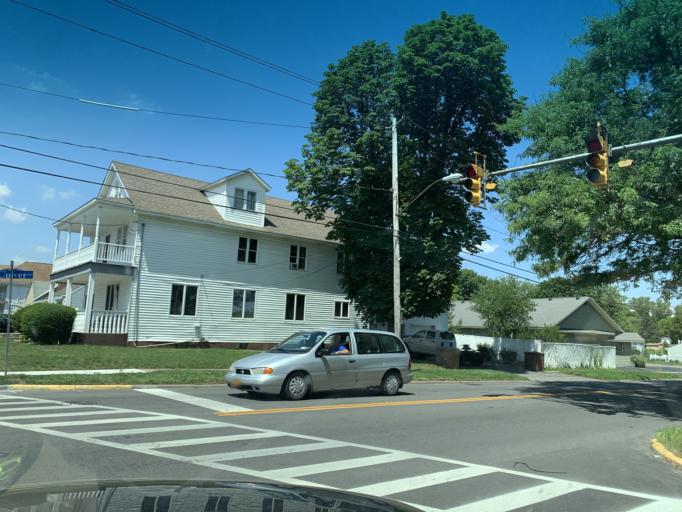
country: US
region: New York
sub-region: Oneida County
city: Utica
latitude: 43.0874
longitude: -75.2001
